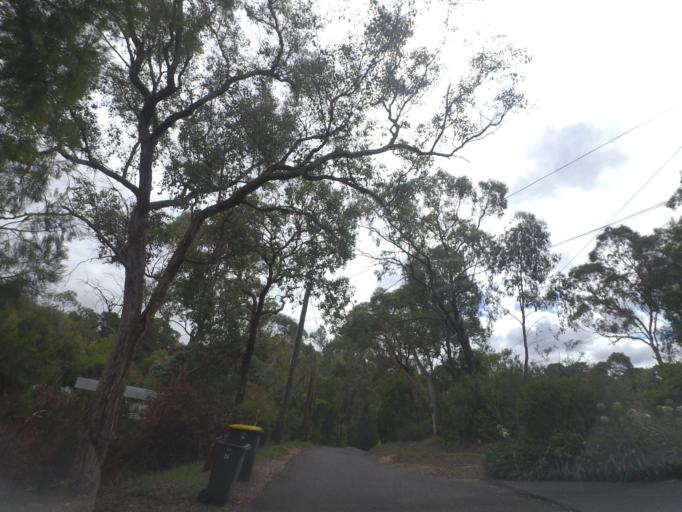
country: AU
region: Victoria
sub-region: Manningham
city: Park Orchards
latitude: -37.7757
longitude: 145.1965
